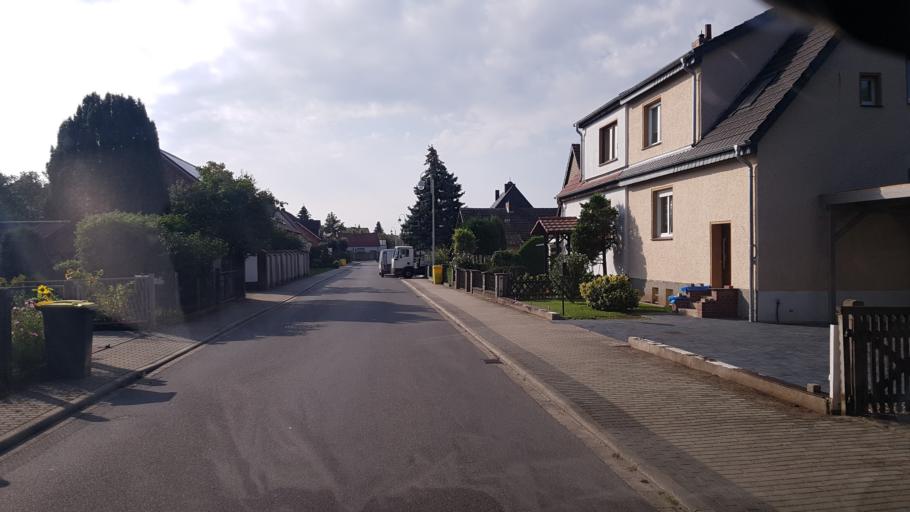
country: DE
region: Brandenburg
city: Luckau
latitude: 51.8540
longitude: 13.7219
